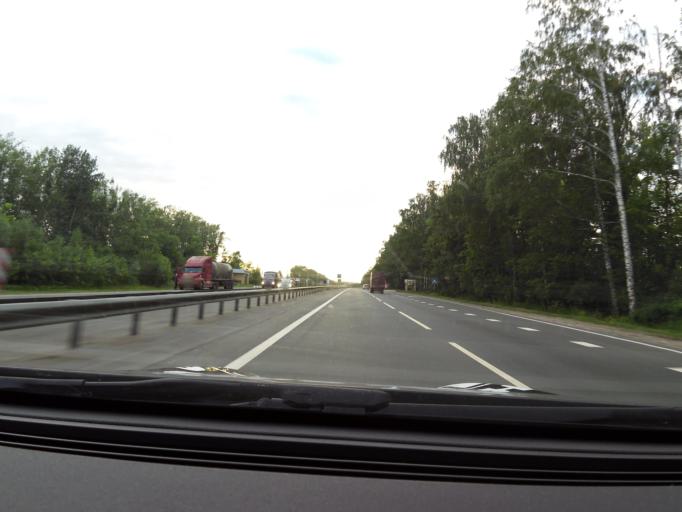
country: RU
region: Chuvashia
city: Kugesi
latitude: 56.0048
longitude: 47.3225
